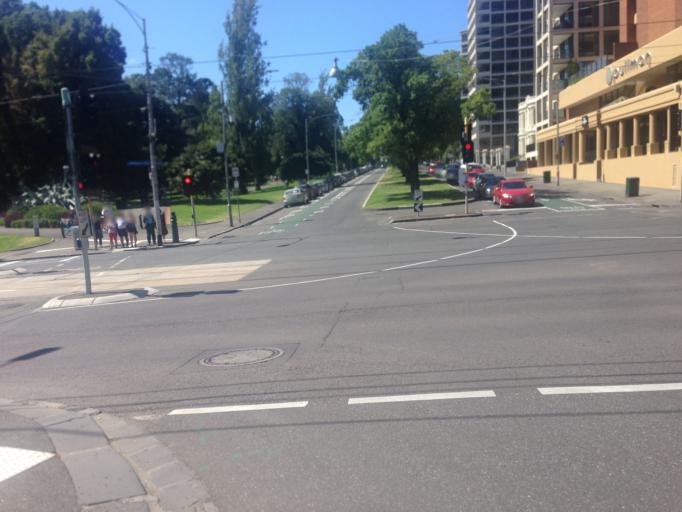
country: AU
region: Victoria
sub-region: Melbourne
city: East Melbourne
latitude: -37.8163
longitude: 144.9826
